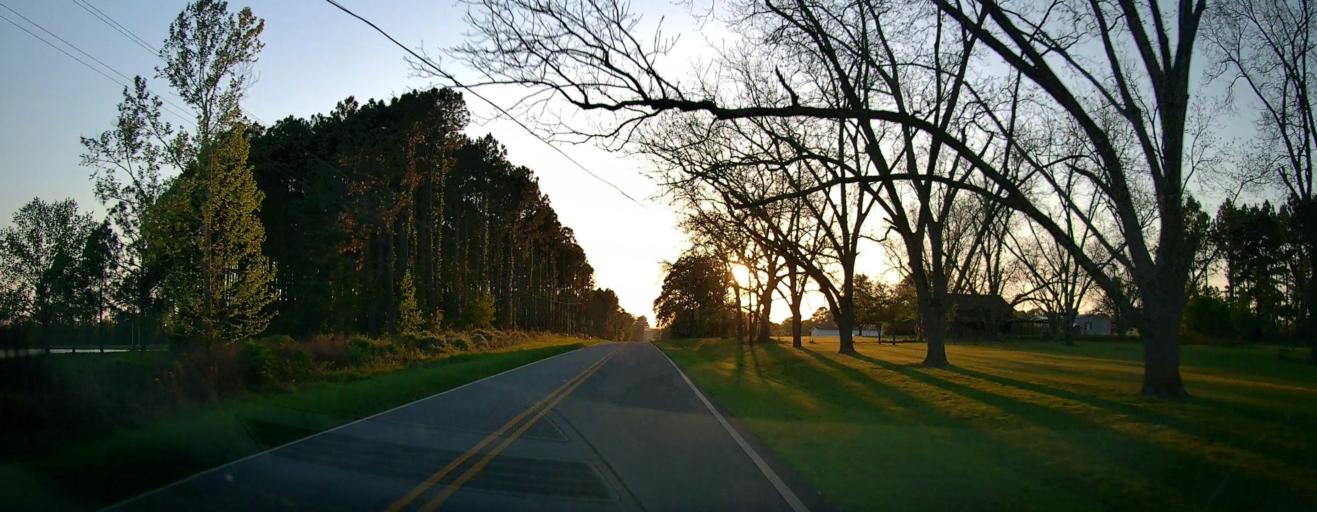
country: US
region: Georgia
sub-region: Ben Hill County
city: Fitzgerald
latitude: 31.7178
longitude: -83.2910
